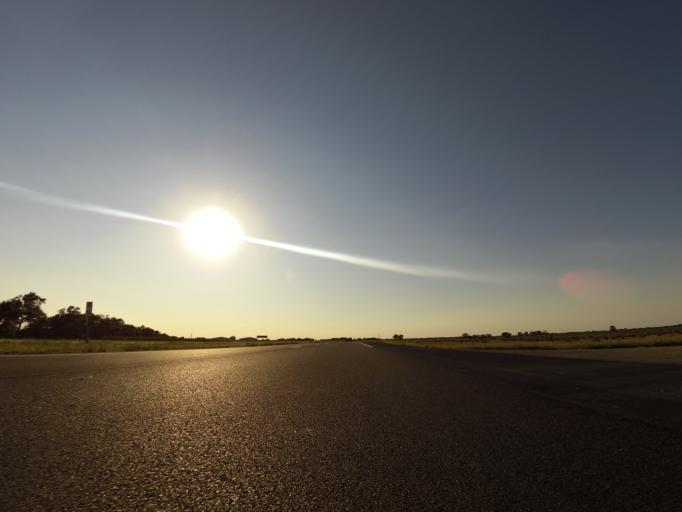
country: US
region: Kansas
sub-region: Reno County
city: Haven
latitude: 37.8766
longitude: -97.7020
